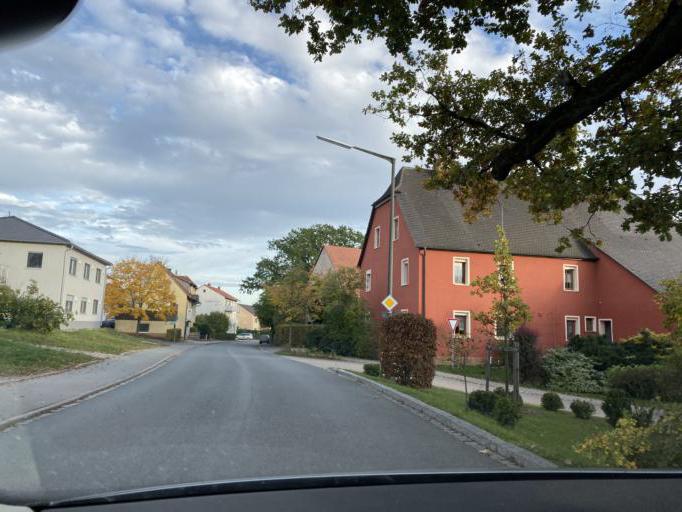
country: DE
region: Bavaria
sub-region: Regierungsbezirk Mittelfranken
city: Puschendorf
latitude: 49.5241
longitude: 10.8277
